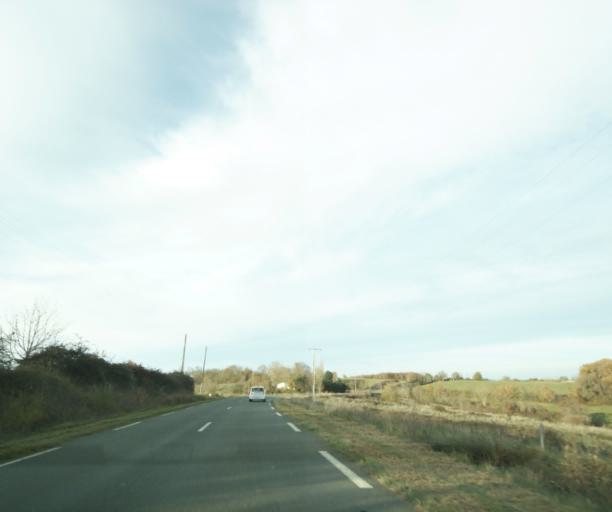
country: FR
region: Midi-Pyrenees
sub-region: Departement du Gers
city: Eauze
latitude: 43.7962
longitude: 0.0991
